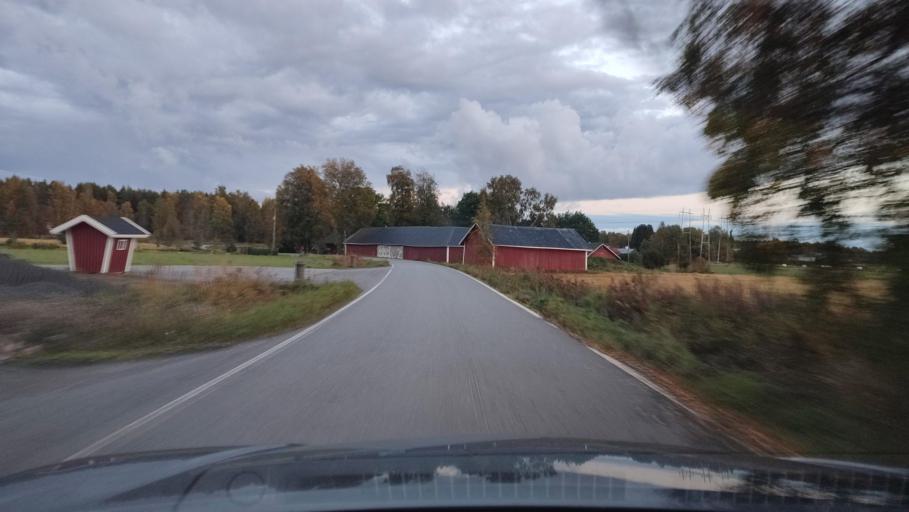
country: FI
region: Ostrobothnia
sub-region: Sydosterbotten
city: Kristinestad
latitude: 62.2729
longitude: 21.5199
